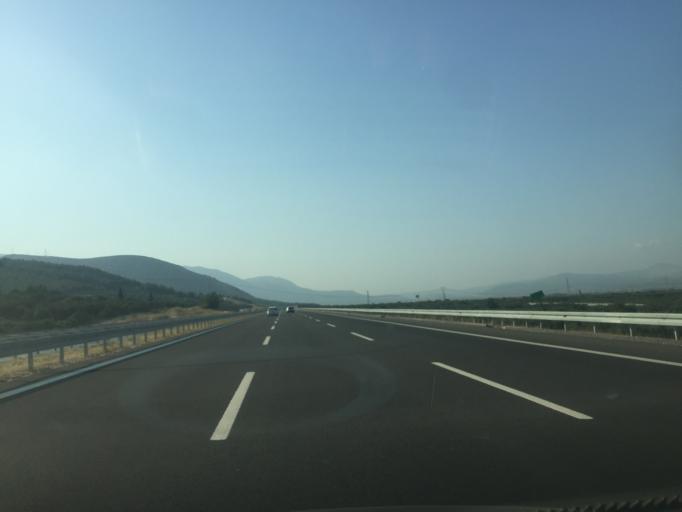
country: TR
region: Manisa
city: Zeytinliova
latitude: 39.0513
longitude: 27.7326
